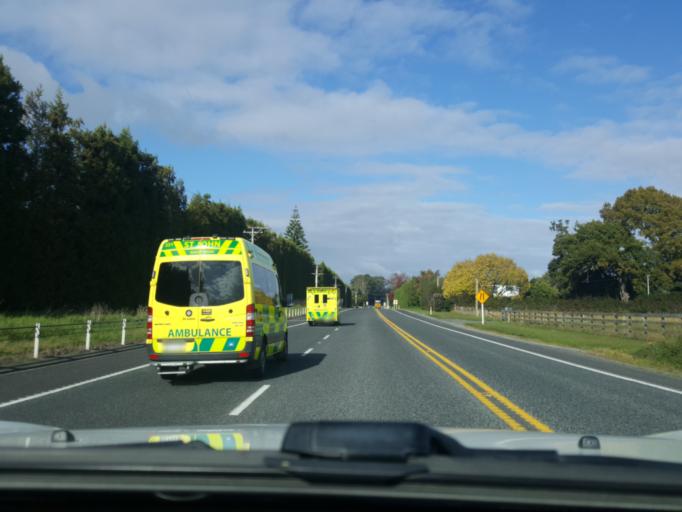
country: NZ
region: Bay of Plenty
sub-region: Western Bay of Plenty District
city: Katikati
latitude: -37.6216
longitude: 175.9519
